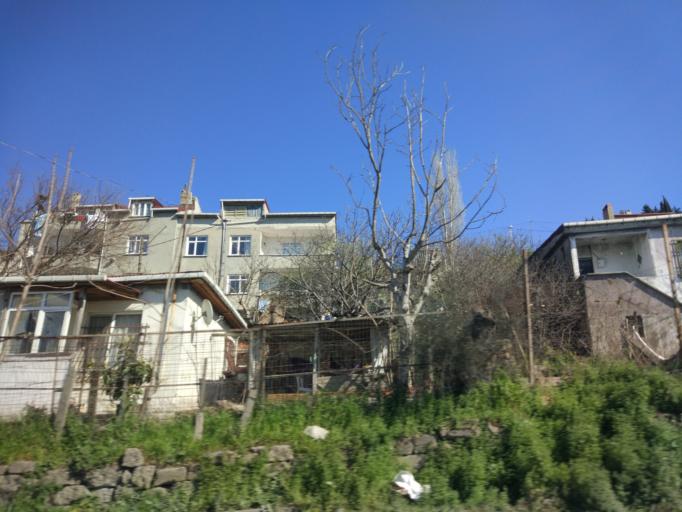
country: TR
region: Istanbul
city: Basaksehir
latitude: 41.0501
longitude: 28.7492
